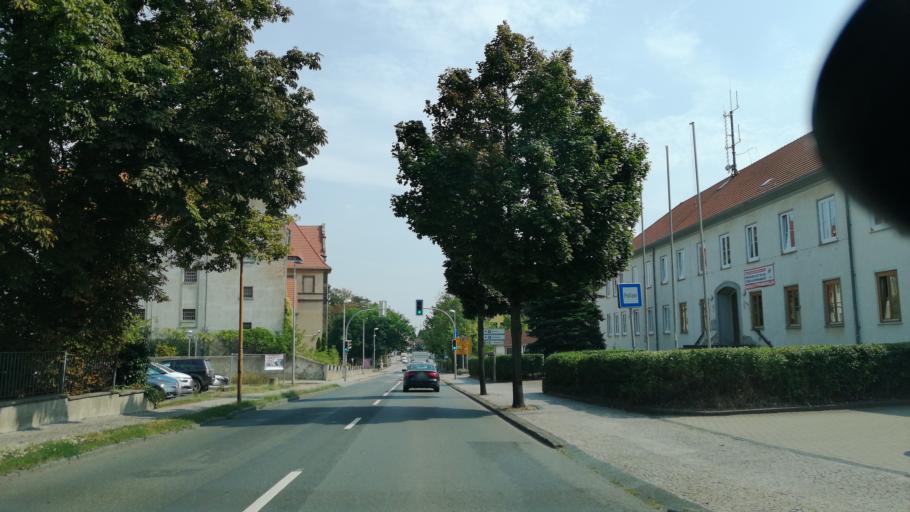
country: DE
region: Saxony-Anhalt
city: Wimmelburg
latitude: 51.5213
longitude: 11.5449
